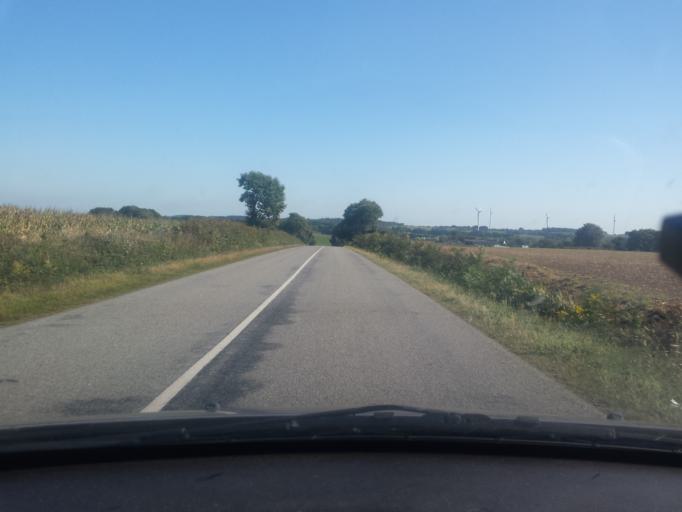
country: FR
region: Brittany
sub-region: Departement du Morbihan
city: Cleguerec
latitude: 48.1210
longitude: -3.1346
